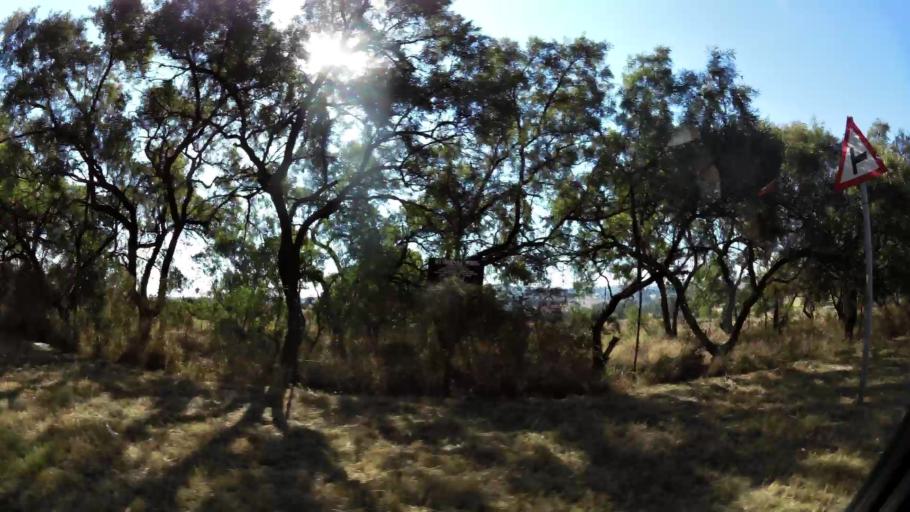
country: ZA
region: Gauteng
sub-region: City of Johannesburg Metropolitan Municipality
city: Midrand
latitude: -26.0195
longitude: 28.0659
